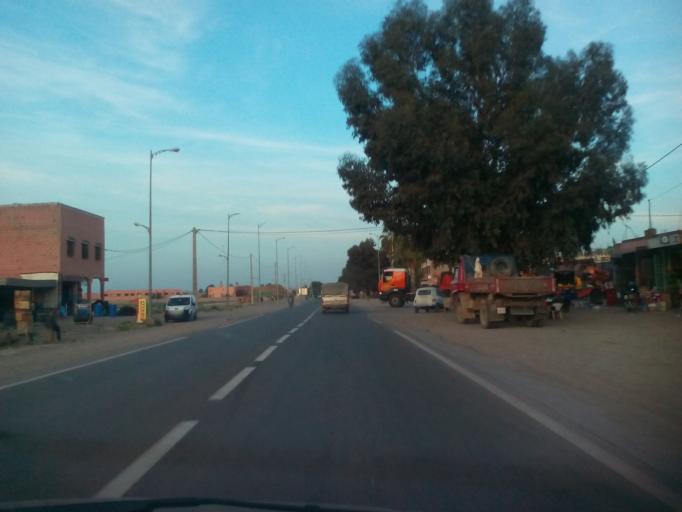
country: MA
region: Marrakech-Tensift-Al Haouz
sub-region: Marrakech
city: Marrakesh
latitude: 31.6304
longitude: -8.2585
